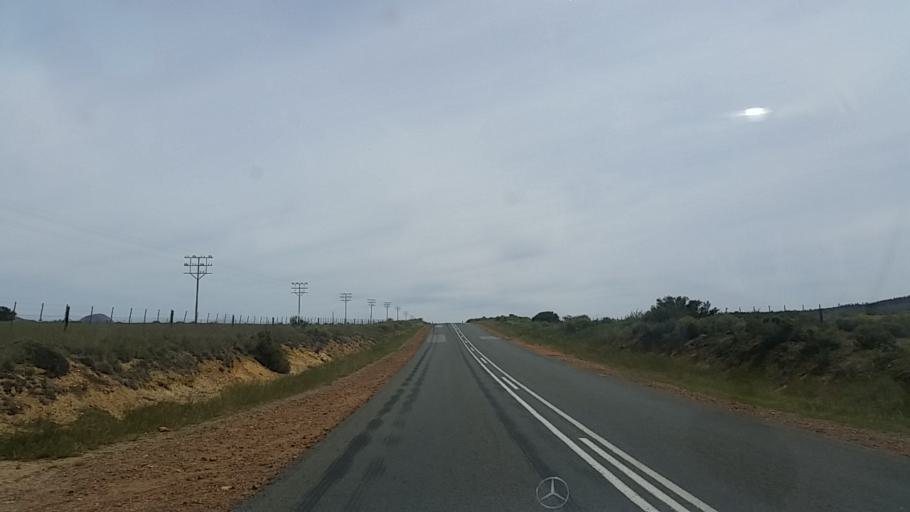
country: ZA
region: Western Cape
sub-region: Eden District Municipality
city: Knysna
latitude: -33.7636
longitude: 22.8348
